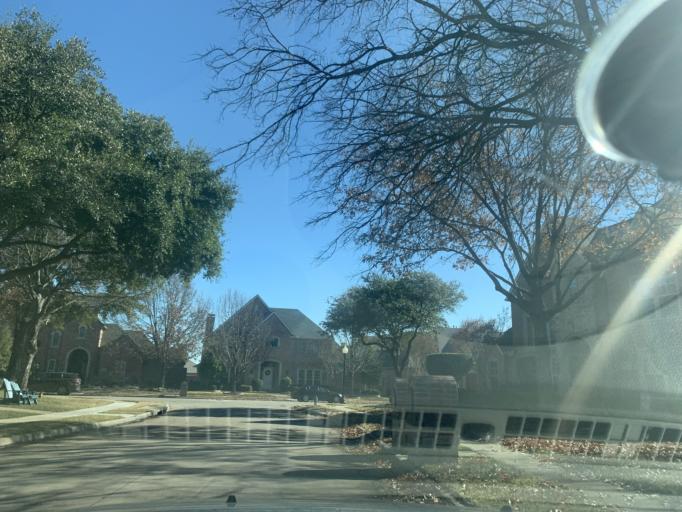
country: US
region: Texas
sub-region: Denton County
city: The Colony
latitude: 33.0543
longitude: -96.8176
